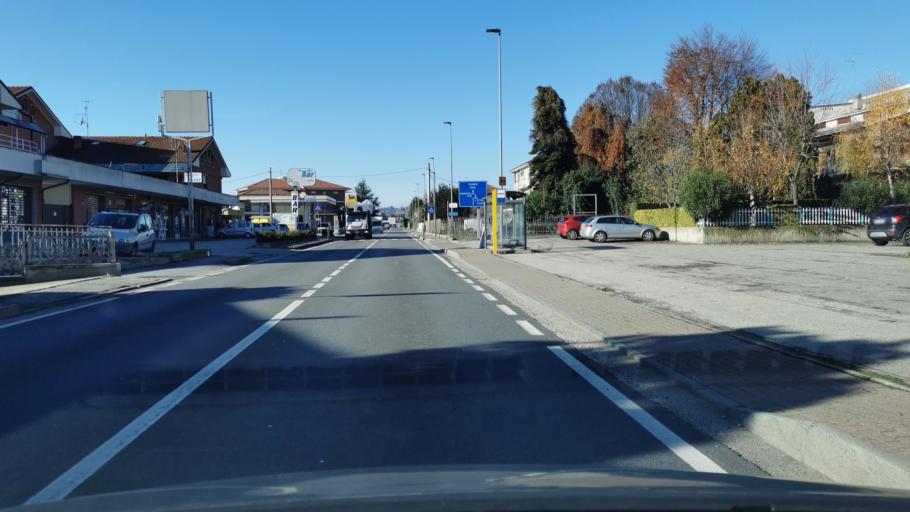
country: IT
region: Piedmont
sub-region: Provincia di Cuneo
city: Cinzano
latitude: 44.6941
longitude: 7.9150
